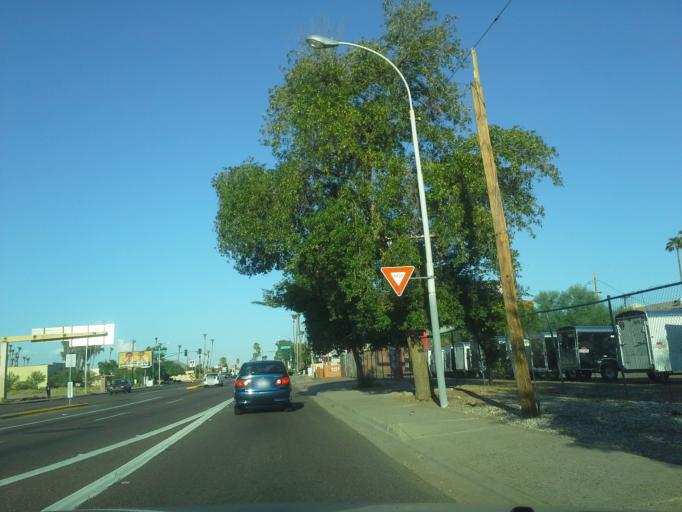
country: US
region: Arizona
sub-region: Maricopa County
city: Glendale
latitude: 33.4948
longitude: -112.1317
